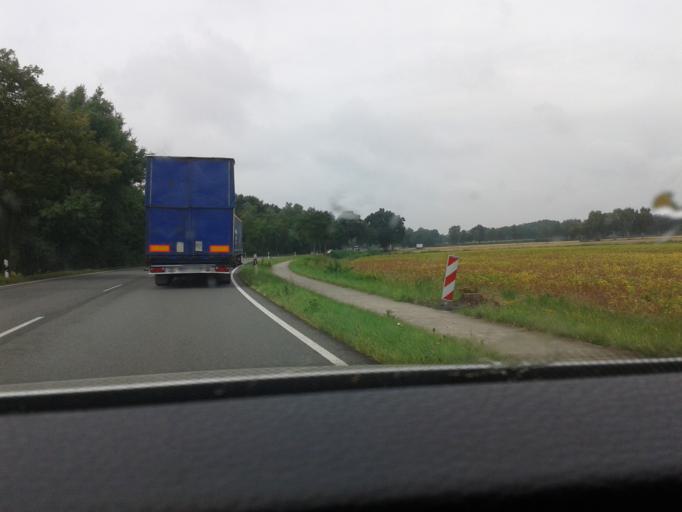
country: DE
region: Lower Saxony
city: Sassenburg
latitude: 52.4801
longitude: 10.6434
